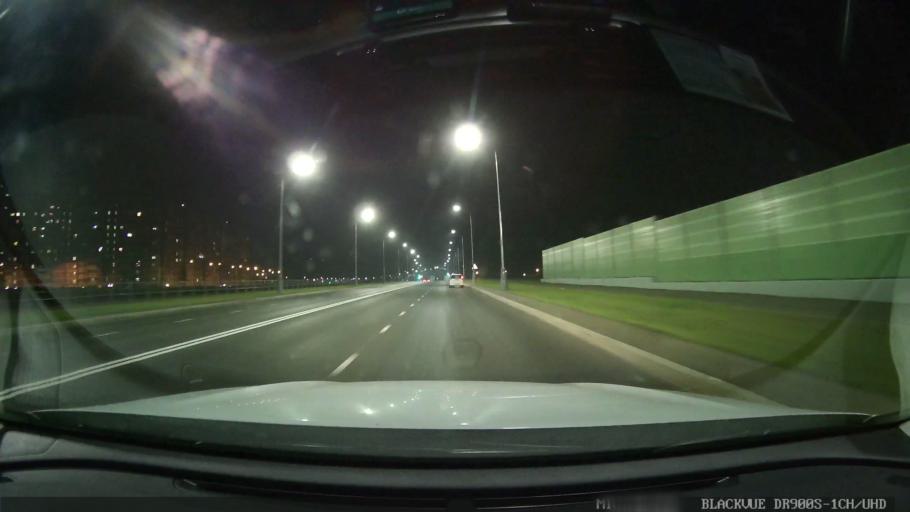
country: RU
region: Moskovskaya
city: Shcherbinka
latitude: 55.5056
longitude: 37.5369
